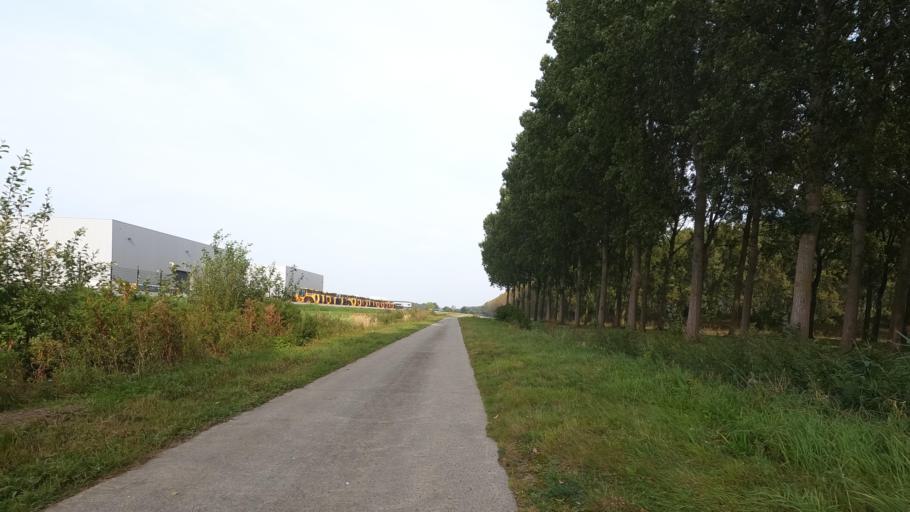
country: BE
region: Flanders
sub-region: Provincie Oost-Vlaanderen
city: Beveren
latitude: 51.2420
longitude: 4.2024
